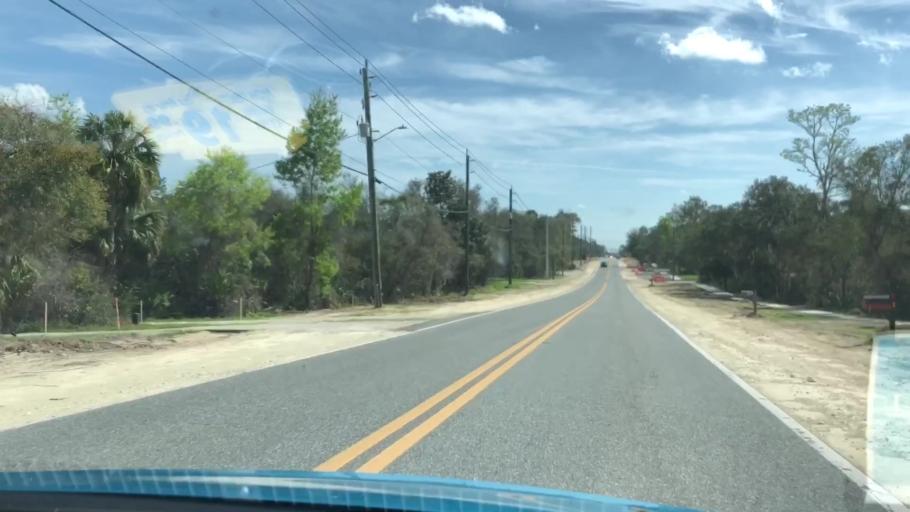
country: US
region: Florida
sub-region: Seminole County
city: Midway
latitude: 28.8584
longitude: -81.1932
